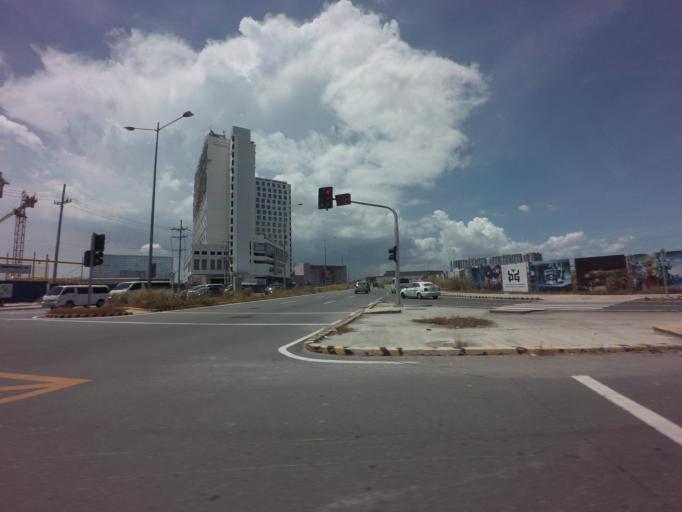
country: PH
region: Metro Manila
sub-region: Makati City
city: Makati City
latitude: 14.5170
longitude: 120.9814
